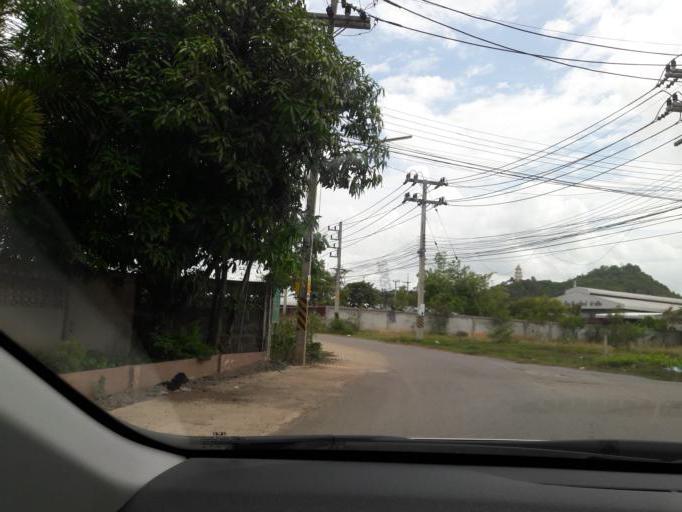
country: TH
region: Ratchaburi
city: Ratchaburi
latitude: 13.5321
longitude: 99.7915
